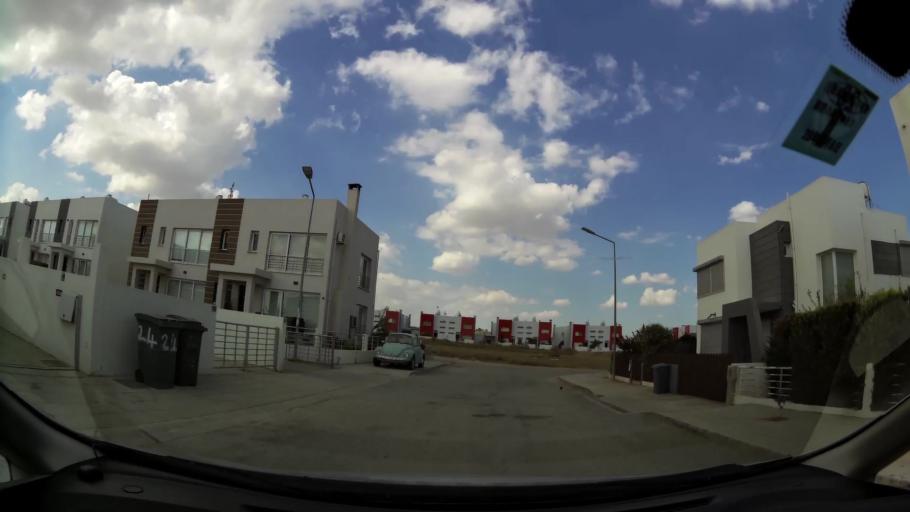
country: CY
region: Lefkosia
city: Nicosia
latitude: 35.2104
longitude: 33.3865
